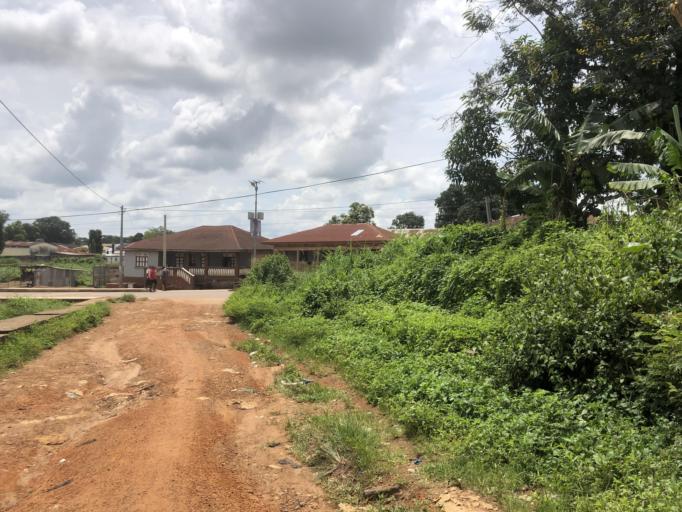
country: SL
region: Northern Province
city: Makeni
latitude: 8.8795
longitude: -12.0483
